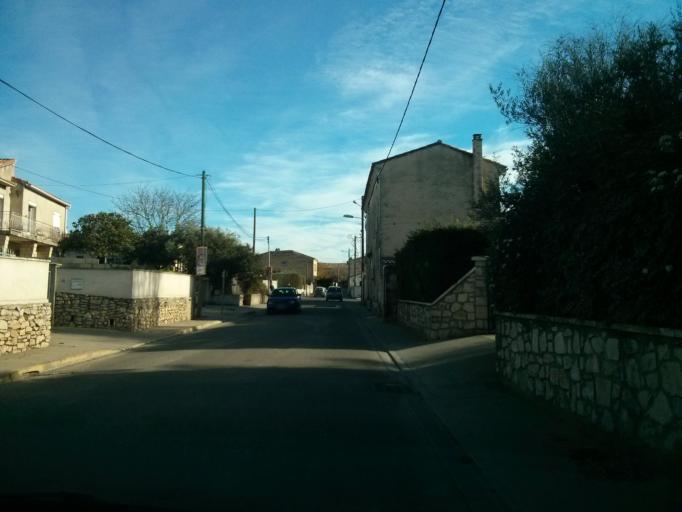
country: FR
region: Languedoc-Roussillon
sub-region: Departement du Gard
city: Vergeze
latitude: 43.7442
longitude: 4.2150
